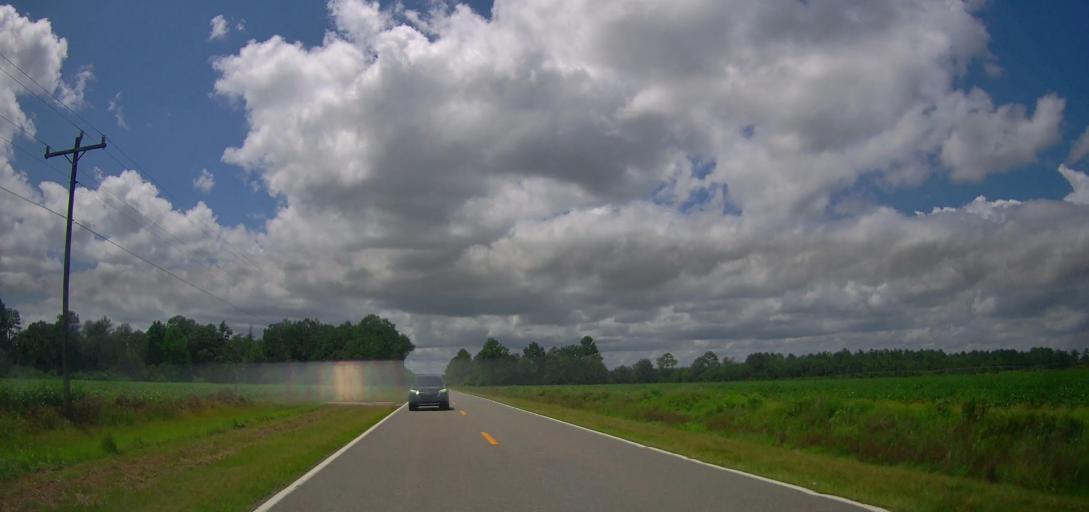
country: US
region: Georgia
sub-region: Irwin County
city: Ocilla
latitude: 31.6465
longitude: -83.2931
